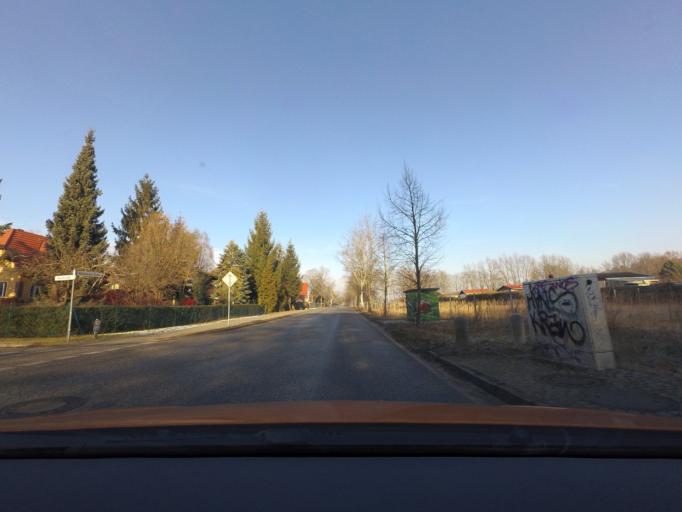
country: DE
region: Berlin
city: Blankenfelde
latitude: 52.6501
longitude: 13.3759
